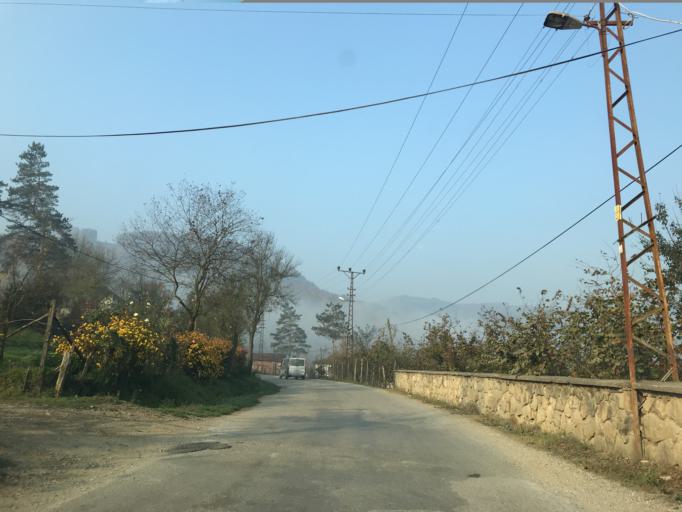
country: TR
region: Duzce
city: Cumayeri
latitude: 40.9129
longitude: 30.9430
